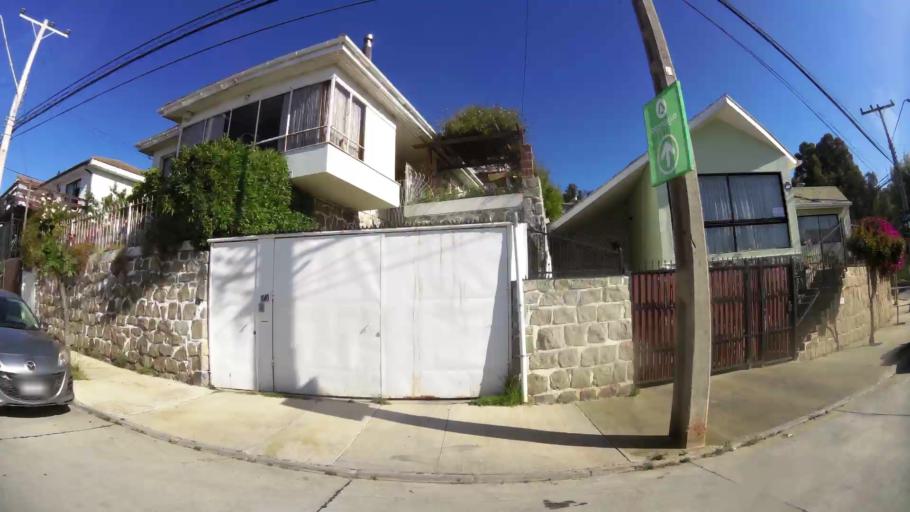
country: CL
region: Valparaiso
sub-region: Provincia de Valparaiso
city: Vina del Mar
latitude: -33.0342
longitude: -71.5604
